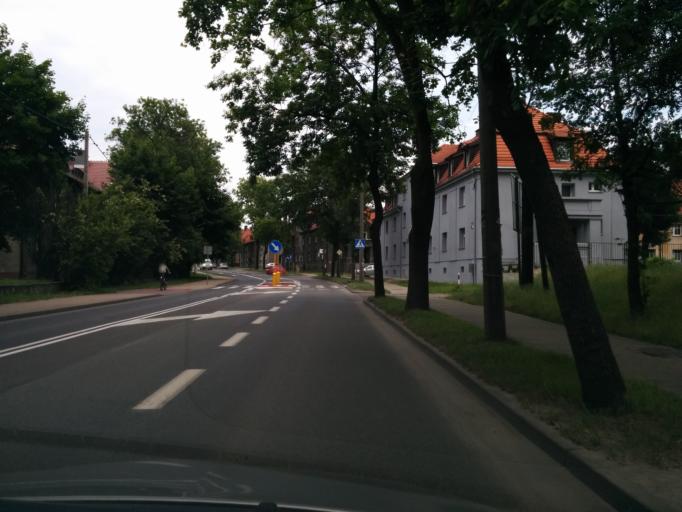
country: PL
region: Silesian Voivodeship
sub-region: Ruda Slaska
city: Ruda Slaska
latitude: 50.2697
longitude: 18.8400
